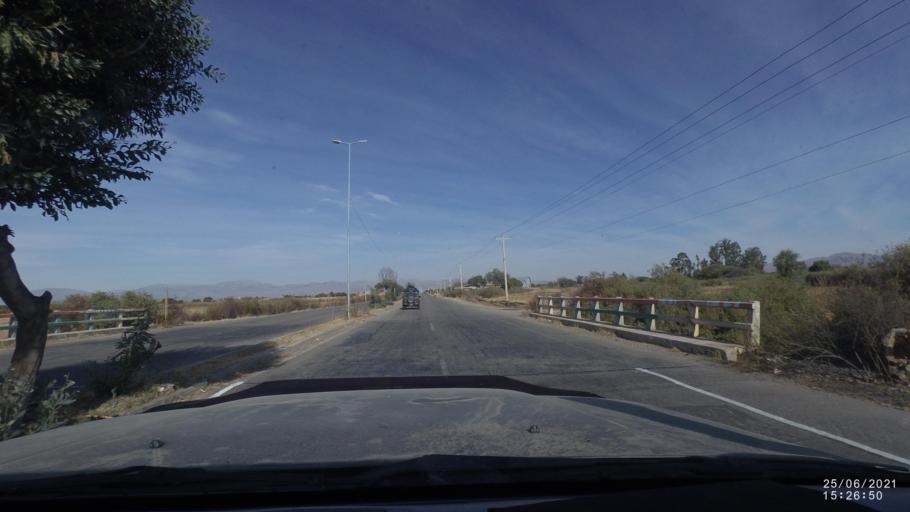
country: BO
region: Cochabamba
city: Cliza
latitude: -17.5428
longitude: -65.9553
